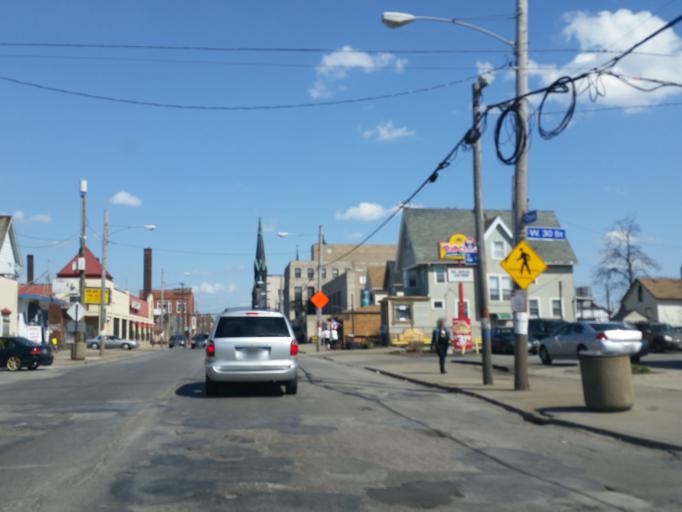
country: US
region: Ohio
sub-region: Cuyahoga County
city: Cleveland
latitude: 41.4699
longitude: -81.7019
